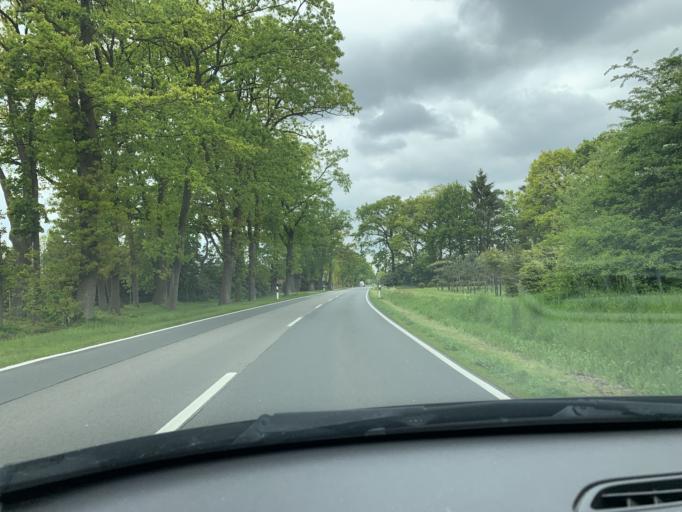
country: DE
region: Lower Saxony
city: Bad Zwischenahn
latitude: 53.1843
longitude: 8.0635
